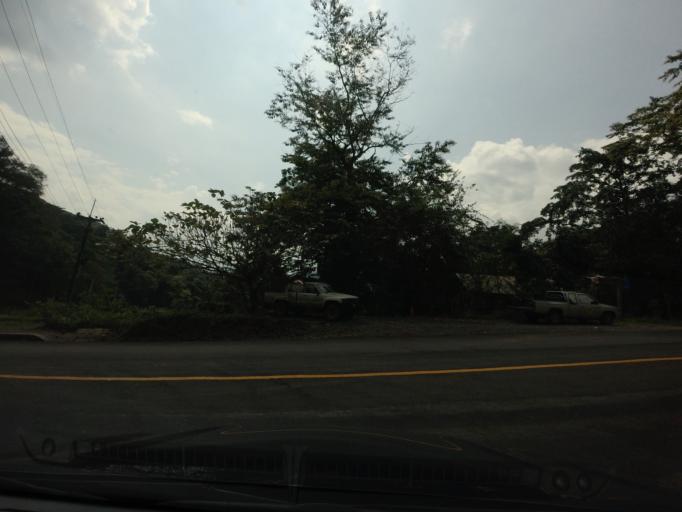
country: TH
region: Nan
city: Bo Kluea
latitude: 19.1833
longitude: 101.1776
